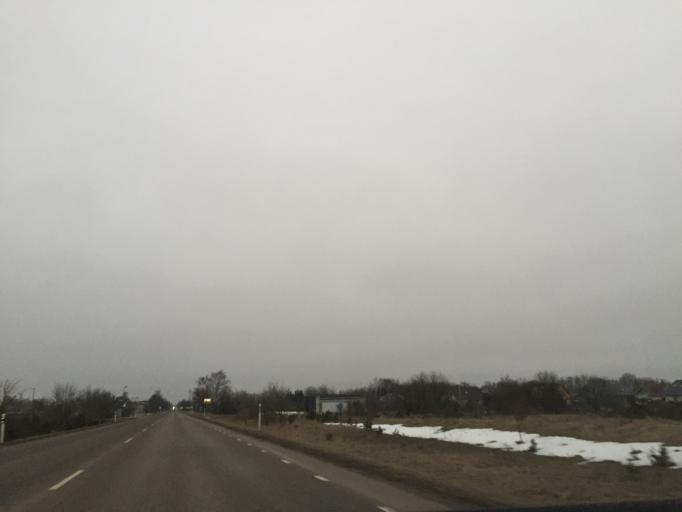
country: EE
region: Saare
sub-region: Kuressaare linn
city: Kuressaare
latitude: 58.2482
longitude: 22.5064
